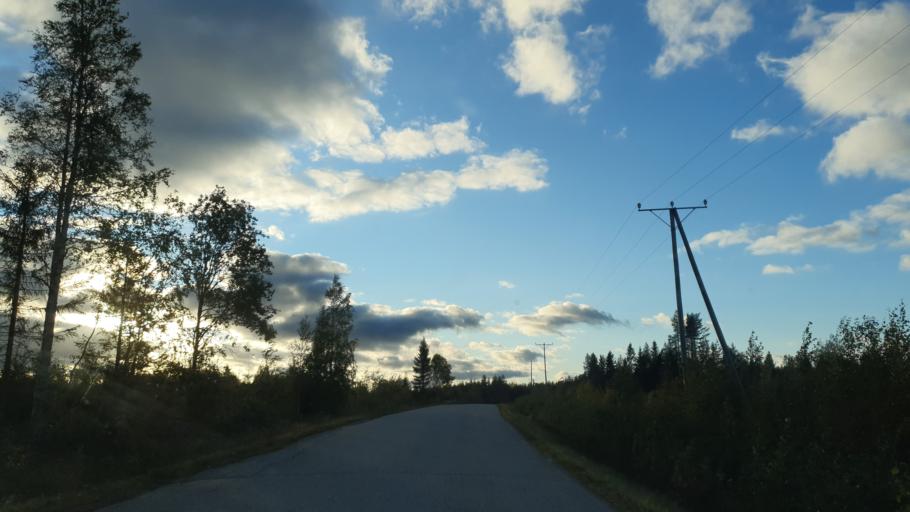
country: FI
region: Kainuu
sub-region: Kehys-Kainuu
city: Kuhmo
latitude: 63.9535
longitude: 29.7405
